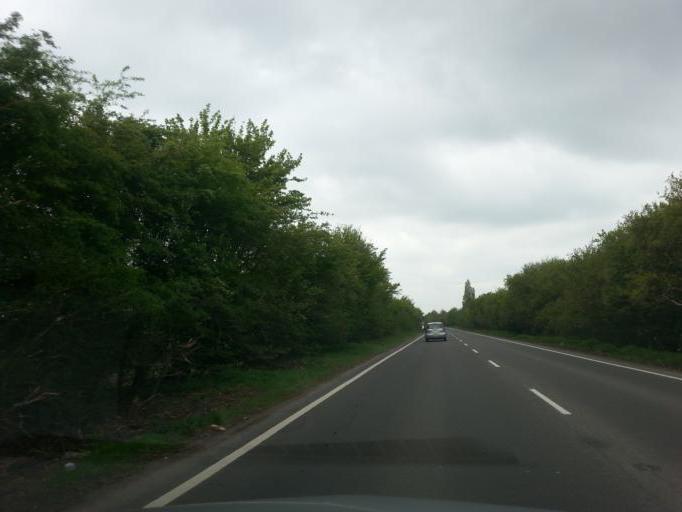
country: GB
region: England
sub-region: Norfolk
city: Emneth
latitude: 52.6287
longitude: 0.2063
